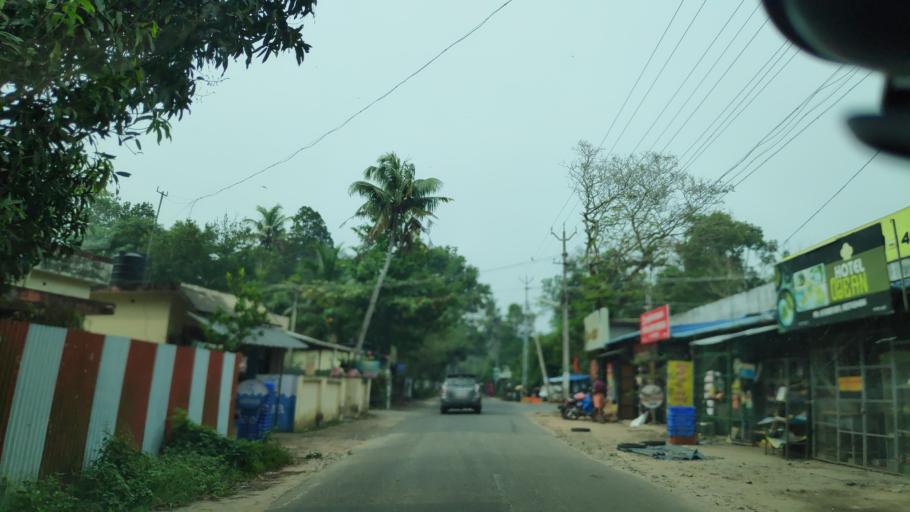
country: IN
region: Kerala
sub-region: Alappuzha
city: Alleppey
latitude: 9.5712
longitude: 76.3371
